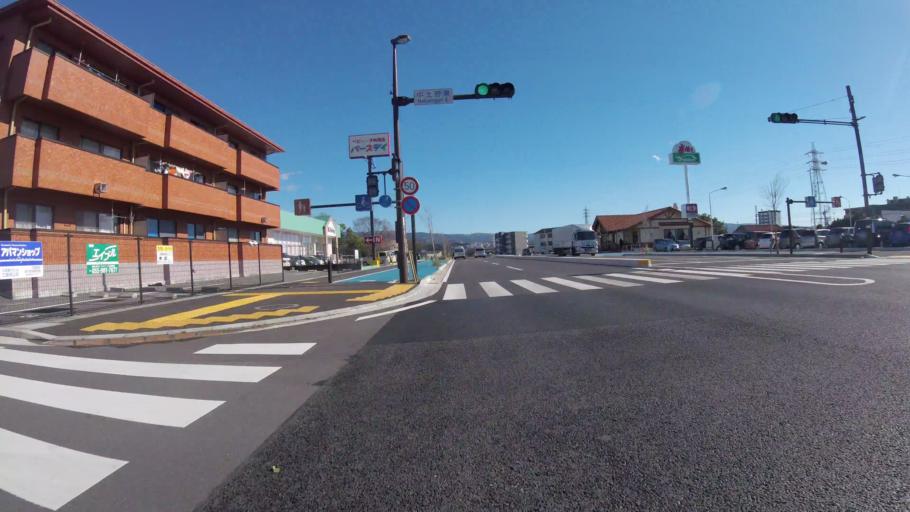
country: JP
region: Shizuoka
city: Mishima
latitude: 35.1390
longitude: 138.9070
